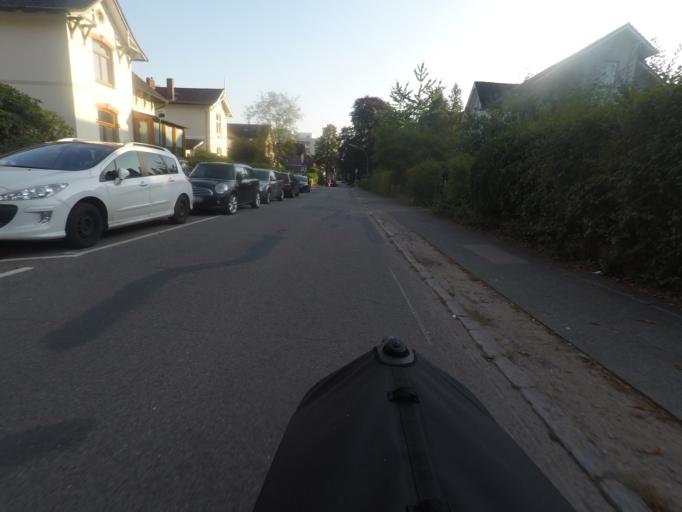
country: DE
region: Schleswig-Holstein
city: Barsbuettel
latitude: 53.6067
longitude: 10.1604
